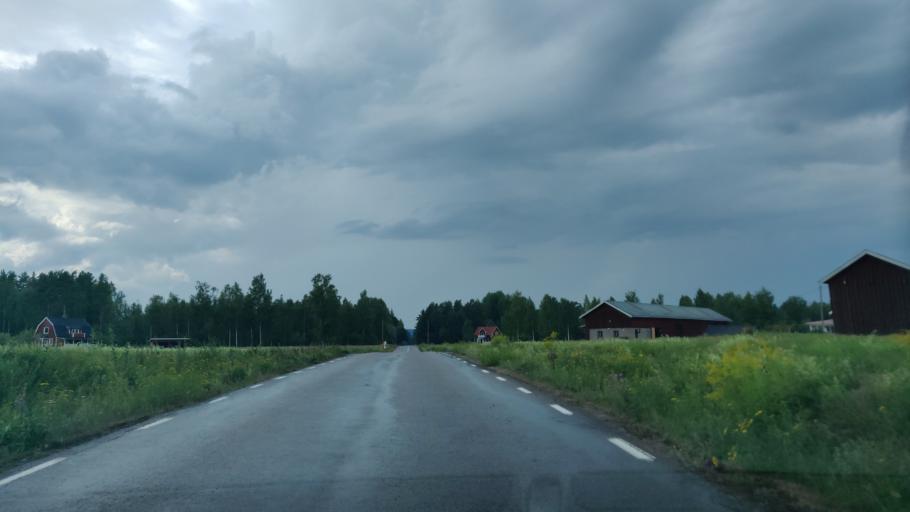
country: SE
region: Vaermland
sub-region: Munkfors Kommun
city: Munkfors
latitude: 59.8694
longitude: 13.5368
